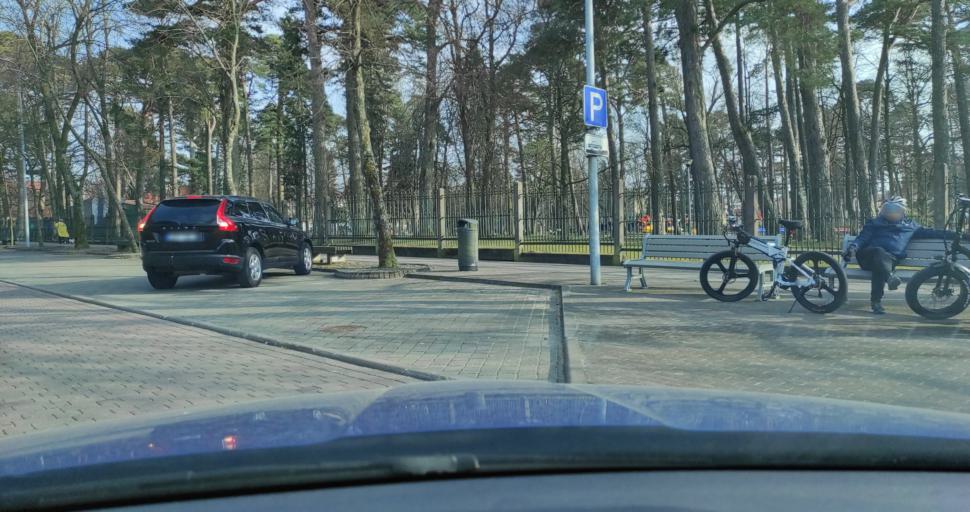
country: LV
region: Ventspils
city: Ventspils
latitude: 57.3897
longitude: 21.5463
